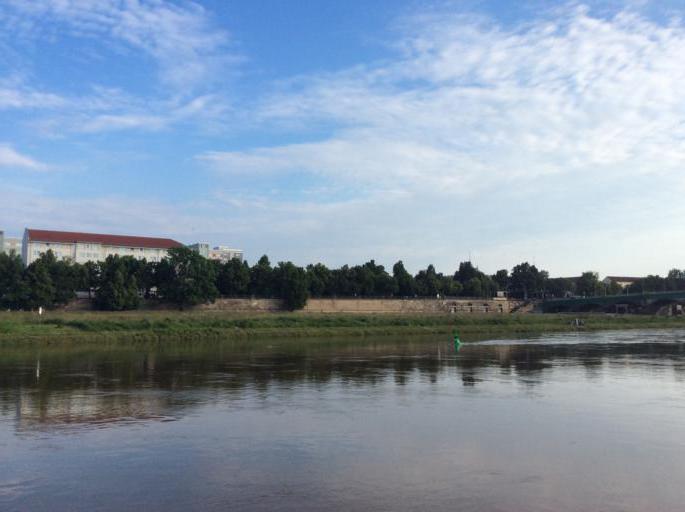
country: DE
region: Saxony
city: Dresden
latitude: 51.0587
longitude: 13.7576
